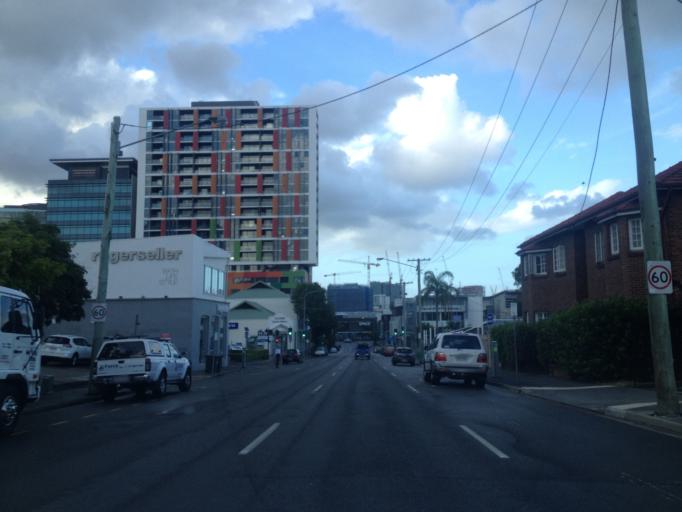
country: AU
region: Queensland
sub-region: Brisbane
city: Fortitude Valley
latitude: -27.4579
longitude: 153.0369
